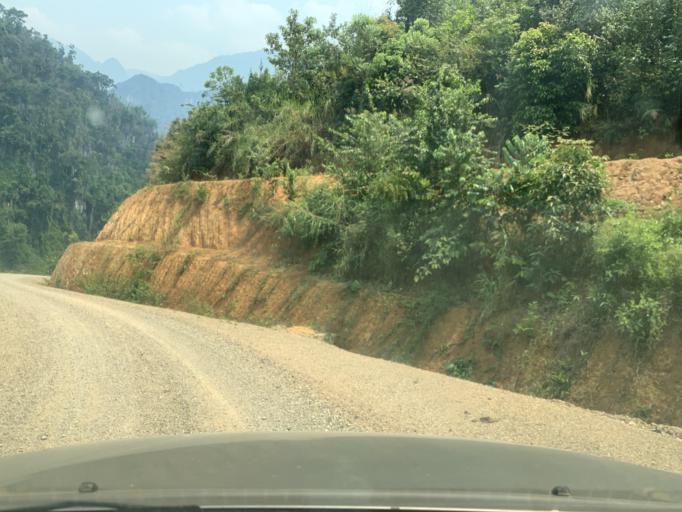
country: LA
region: Louangphabang
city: Louangphabang
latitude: 19.8596
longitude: 102.2567
